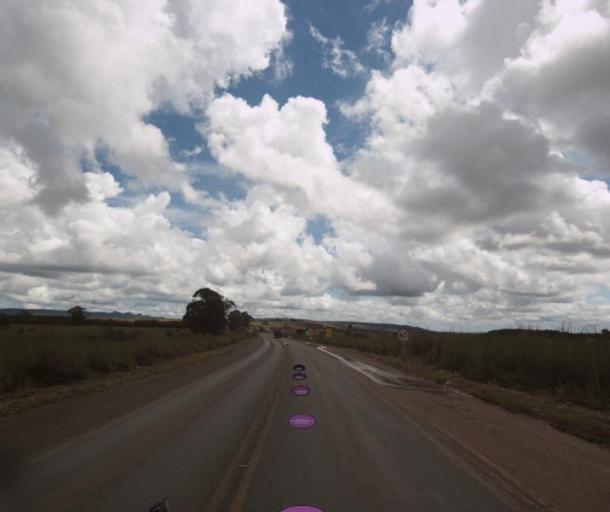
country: BR
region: Goias
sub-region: Pirenopolis
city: Pirenopolis
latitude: -15.7547
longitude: -48.7466
